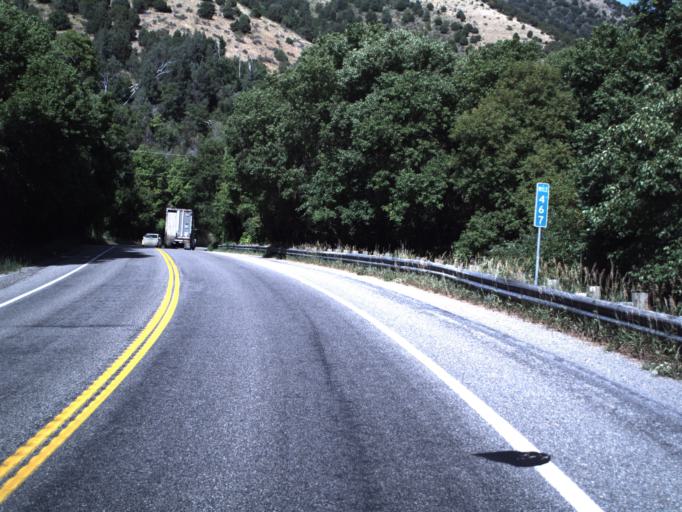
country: US
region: Utah
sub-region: Cache County
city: North Logan
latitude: 41.7635
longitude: -111.6934
